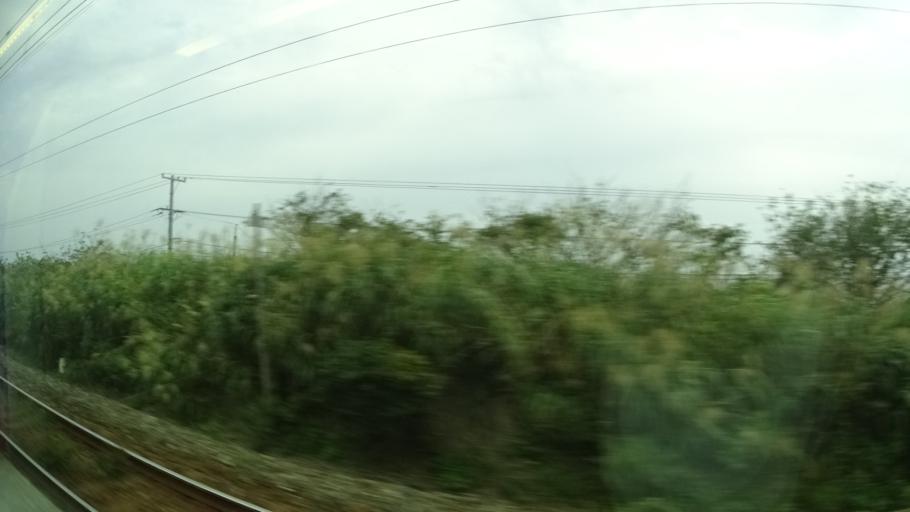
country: JP
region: Yamagata
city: Tsuruoka
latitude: 38.6564
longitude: 139.6042
